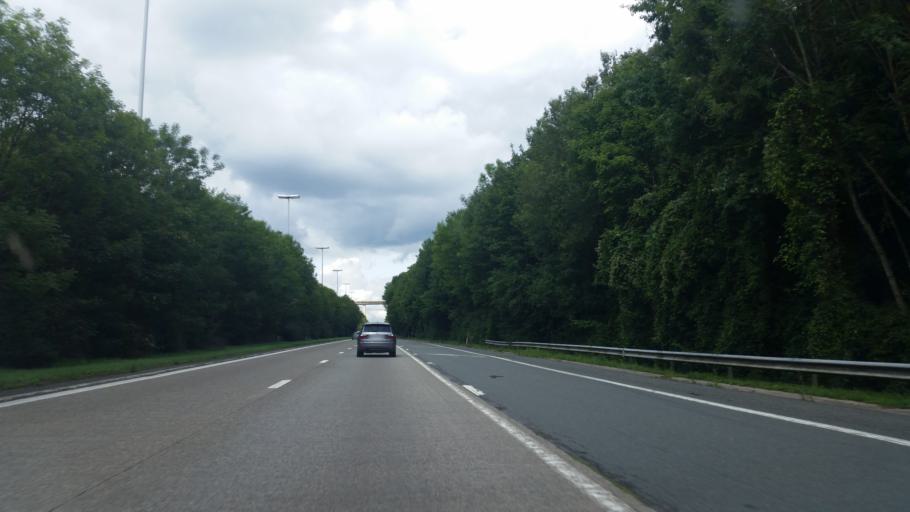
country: BE
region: Wallonia
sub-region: Province de Namur
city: Assesse
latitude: 50.3376
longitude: 5.0146
